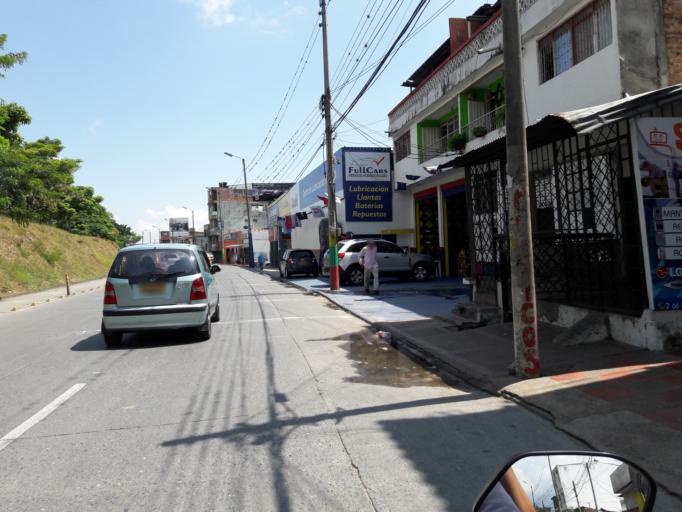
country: CO
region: Tolima
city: Ibague
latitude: 4.4351
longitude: -75.2197
